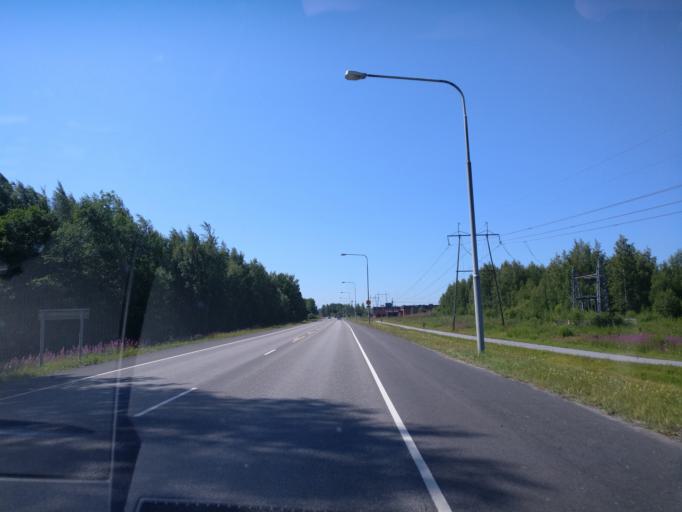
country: FI
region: Satakunta
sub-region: Pori
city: Ulvila
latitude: 61.4562
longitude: 21.8692
